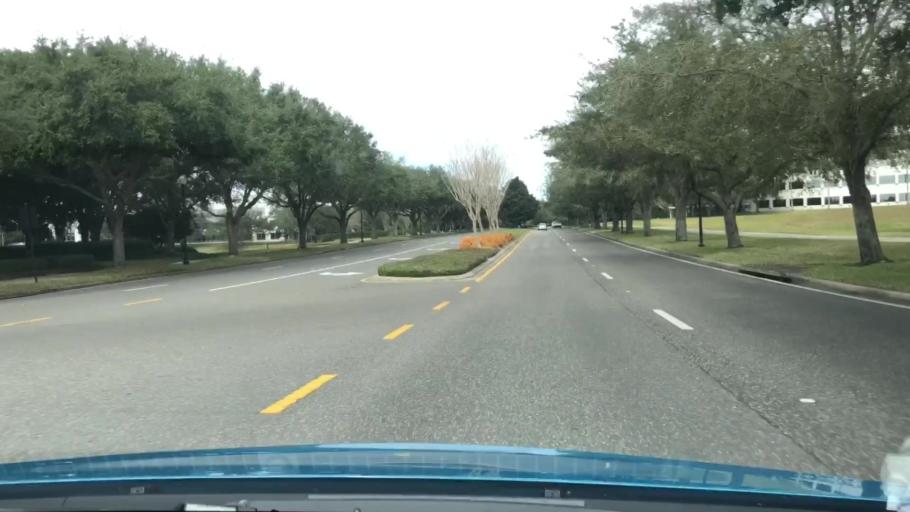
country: US
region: Florida
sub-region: Seminole County
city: Heathrow
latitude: 28.7727
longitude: -81.3588
